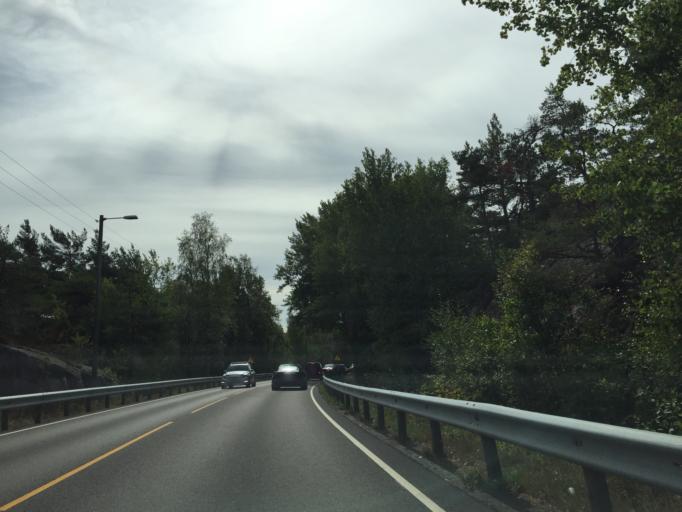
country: NO
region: Ostfold
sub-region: Fredrikstad
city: Fredrikstad
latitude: 59.1510
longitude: 10.9402
